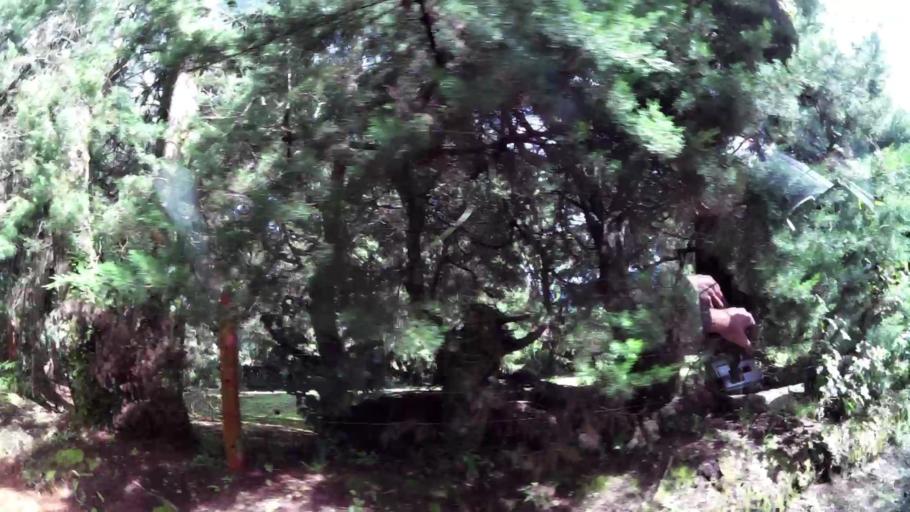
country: PA
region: Chiriqui
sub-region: Distrito Boquete
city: Boquete
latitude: 8.7969
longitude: -82.4336
